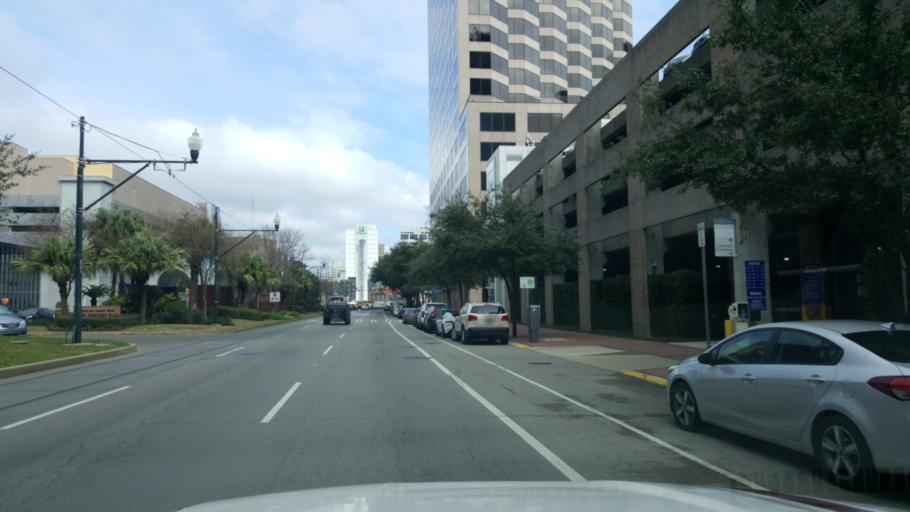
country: US
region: Louisiana
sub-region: Orleans Parish
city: New Orleans
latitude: 29.9487
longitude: -90.0761
